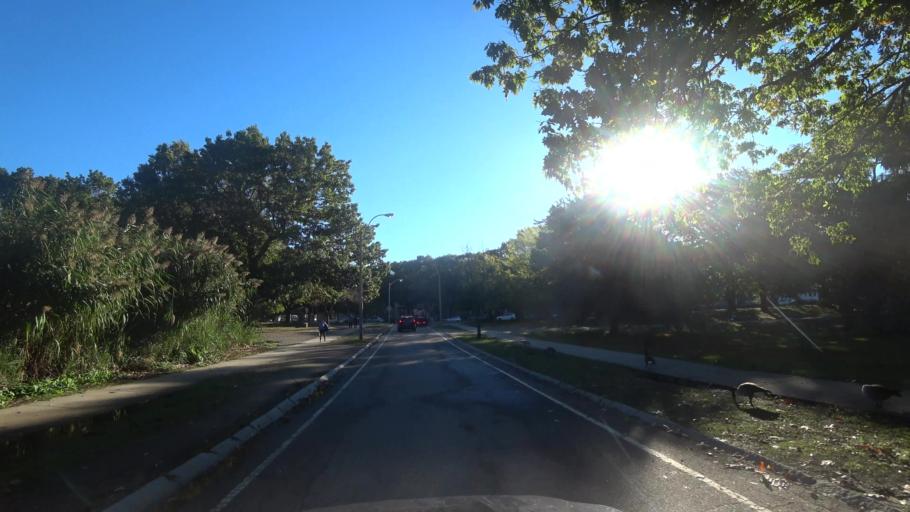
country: US
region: Massachusetts
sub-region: Norfolk County
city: Brookline
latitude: 42.3432
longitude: -71.0926
